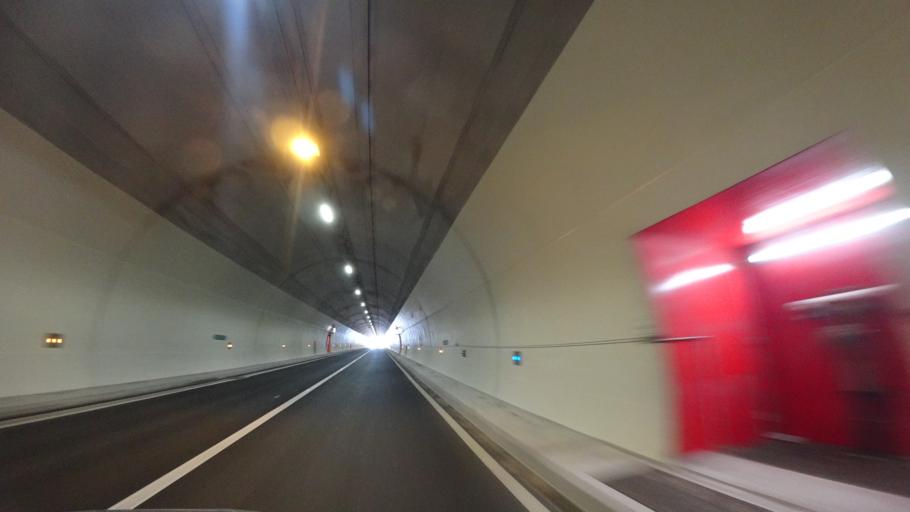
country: FR
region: Corsica
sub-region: Departement de la Corse-du-Sud
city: Propriano
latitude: 41.6717
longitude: 8.9274
